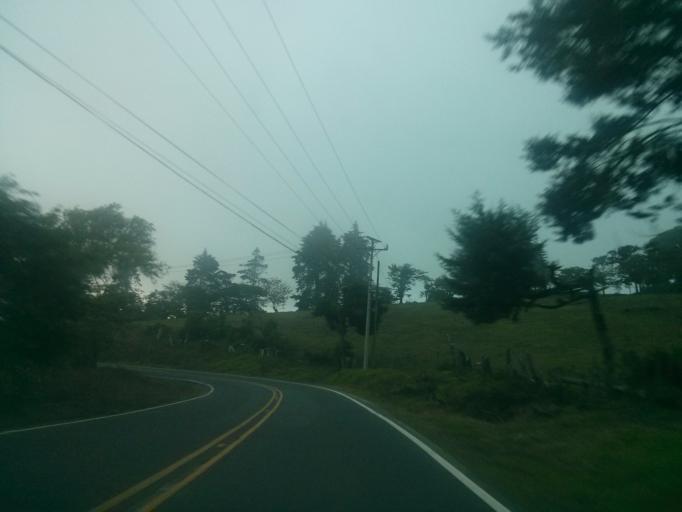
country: CR
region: Cartago
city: Cot
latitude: 9.8905
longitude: -83.8570
